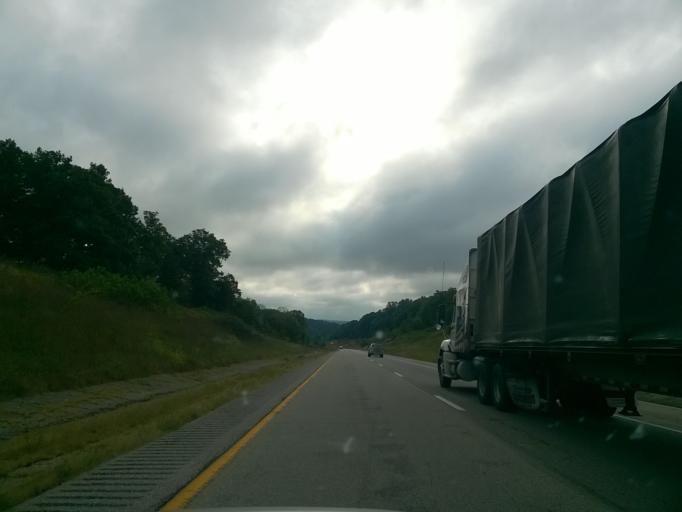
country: US
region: Indiana
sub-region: Crawford County
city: English
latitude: 38.2442
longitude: -86.4220
